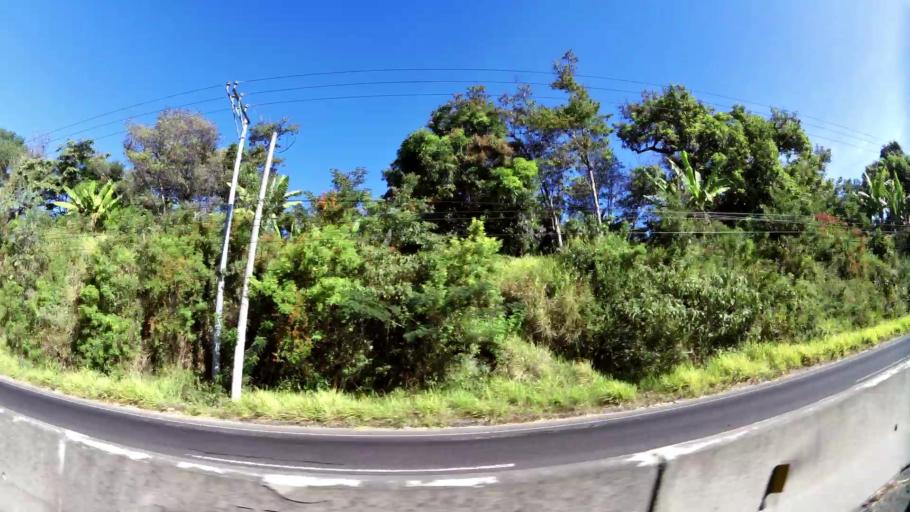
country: SV
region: Santa Ana
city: Coatepeque
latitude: 13.9396
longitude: -89.5342
